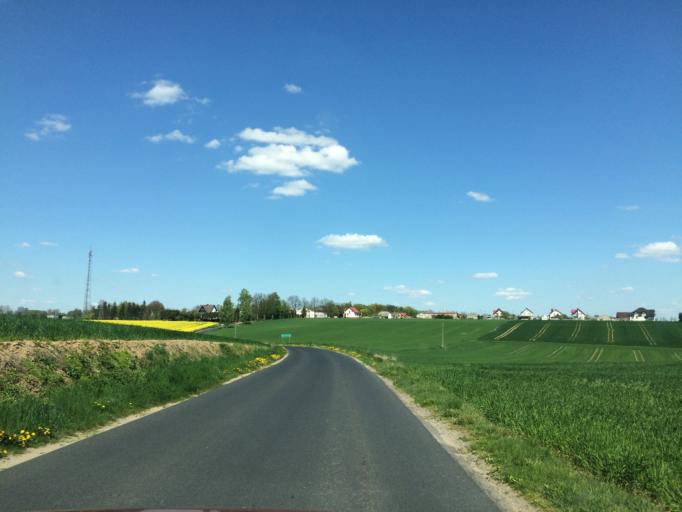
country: PL
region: Warmian-Masurian Voivodeship
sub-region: Powiat ilawski
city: Lubawa
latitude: 53.4053
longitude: 19.7492
